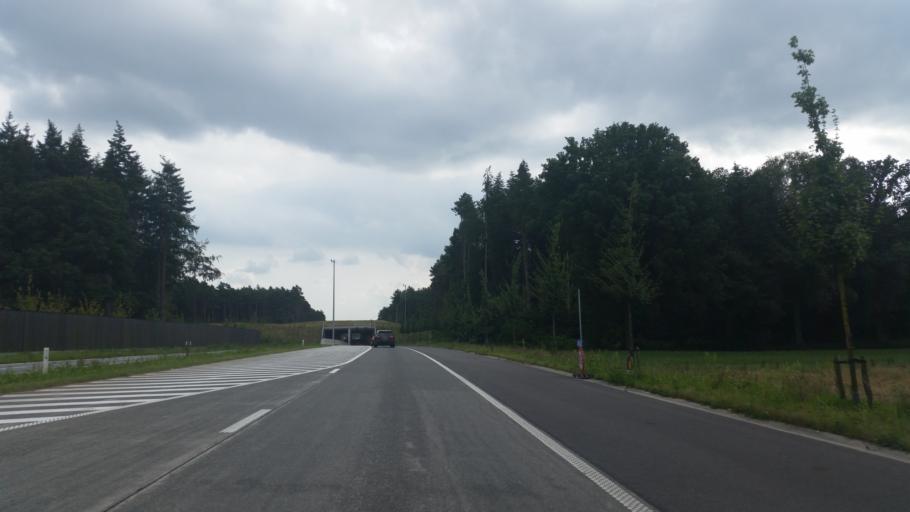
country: BE
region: Flanders
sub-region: Provincie Antwerpen
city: Kasterlee
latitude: 51.2363
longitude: 4.9575
